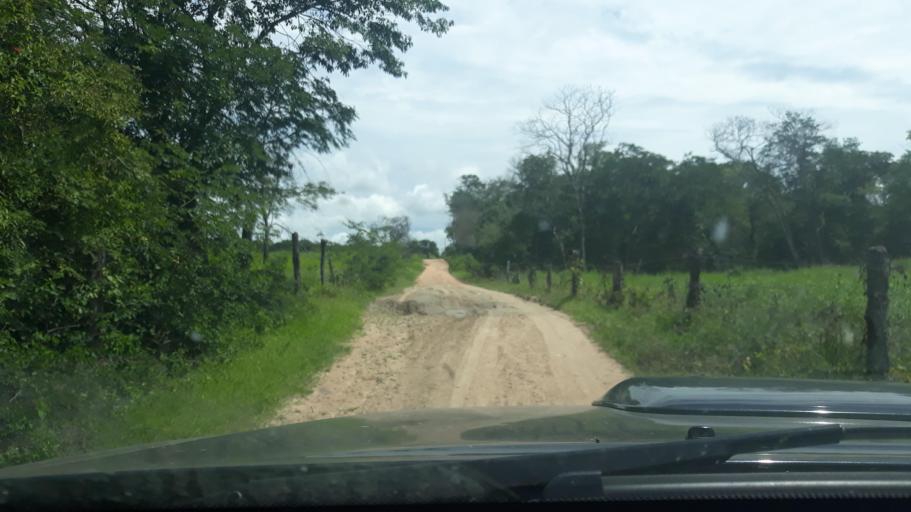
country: BR
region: Bahia
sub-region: Riacho De Santana
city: Riacho de Santana
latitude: -13.8657
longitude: -43.0179
